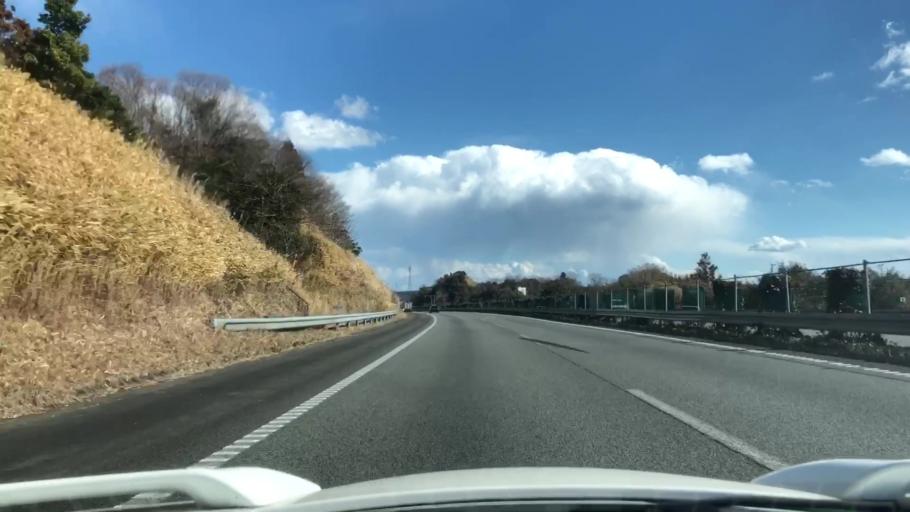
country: JP
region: Shizuoka
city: Kakegawa
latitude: 34.7572
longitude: 138.0577
